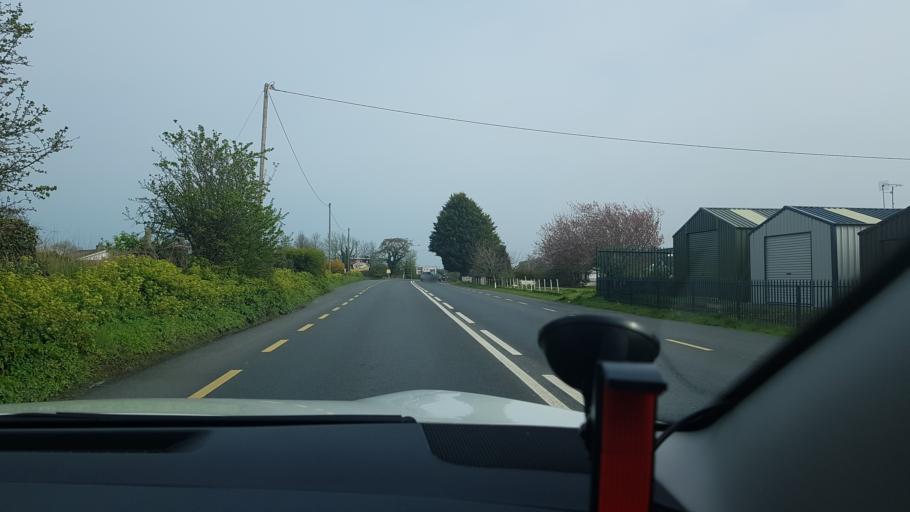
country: IE
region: Leinster
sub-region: An Mhi
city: Stamullin
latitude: 53.6594
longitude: -6.2658
